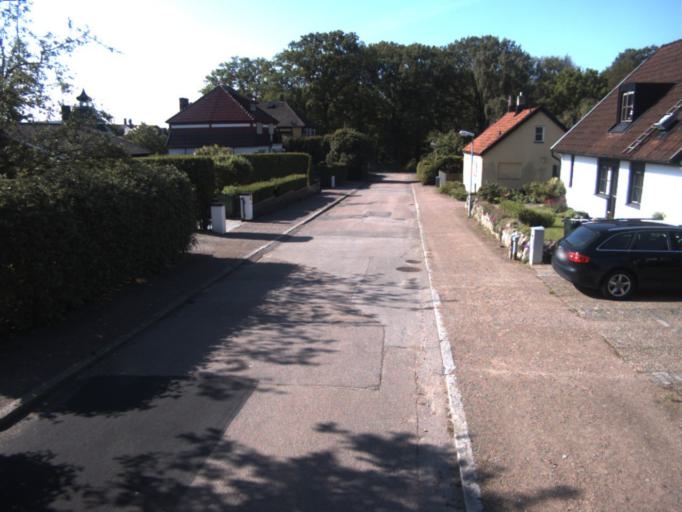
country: SE
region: Skane
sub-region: Helsingborg
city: Rydeback
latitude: 56.0243
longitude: 12.7516
